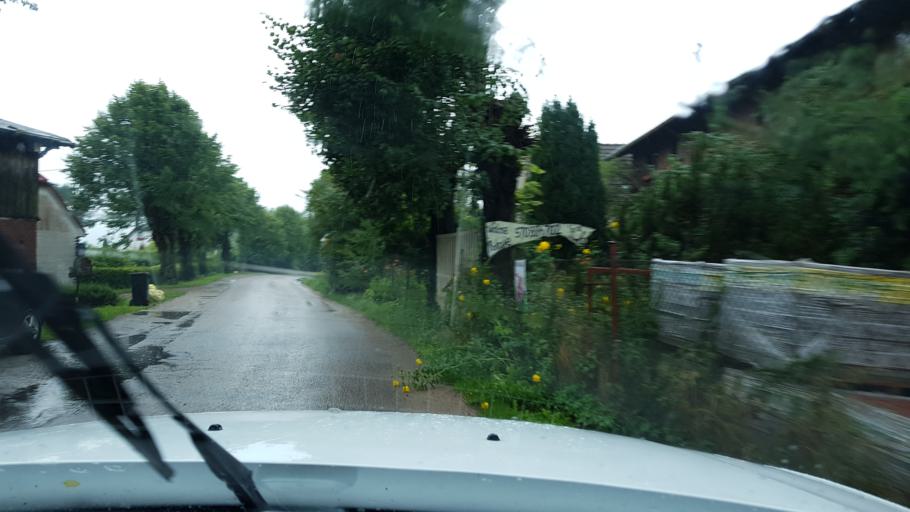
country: PL
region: West Pomeranian Voivodeship
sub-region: Powiat kolobrzeski
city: Ustronie Morskie
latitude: 54.2131
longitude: 15.8884
